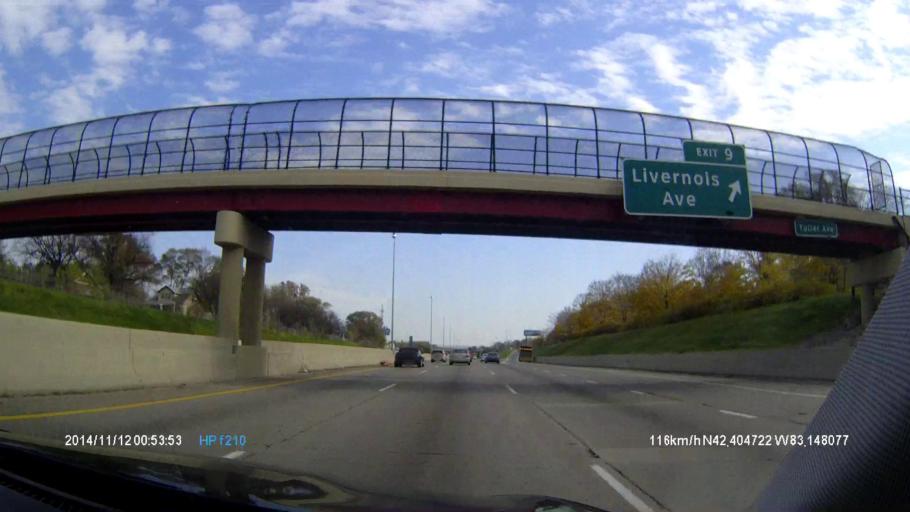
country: US
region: Michigan
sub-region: Wayne County
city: Highland Park
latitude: 42.4047
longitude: -83.1479
